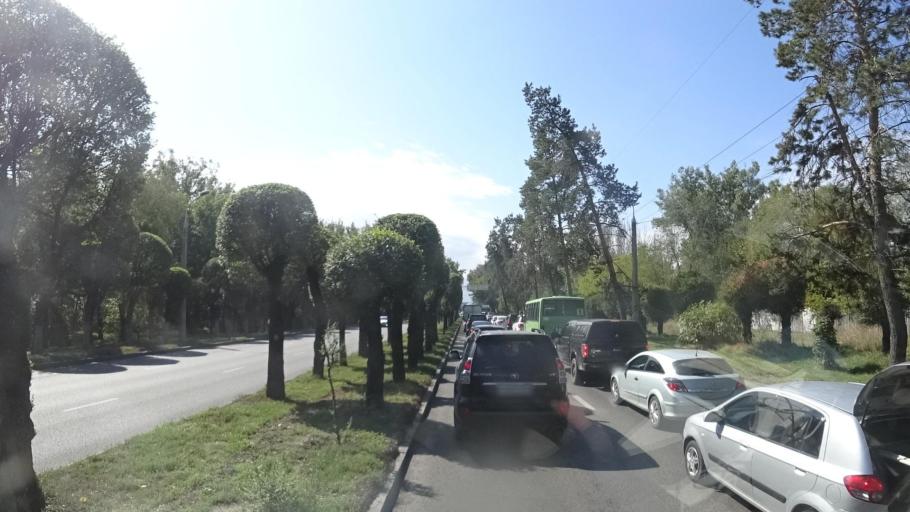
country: KZ
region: Almaty Oblysy
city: Pervomayskiy
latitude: 43.3237
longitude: 76.9739
